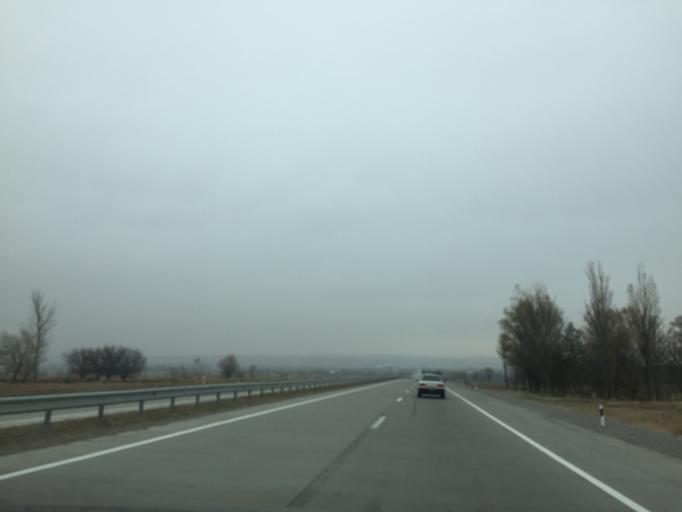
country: KZ
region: Ongtustik Qazaqstan
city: Aksu
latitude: 42.4683
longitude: 69.7942
